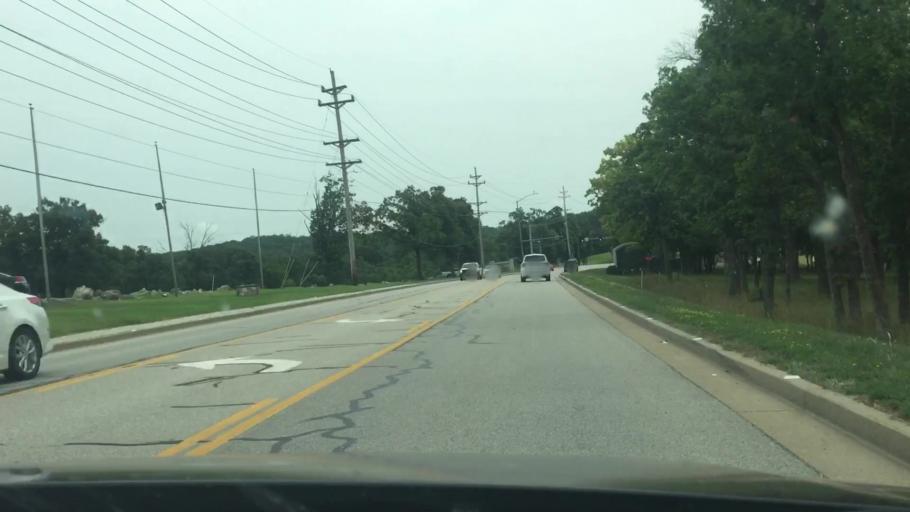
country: US
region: Missouri
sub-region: Camden County
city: Four Seasons
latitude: 38.1913
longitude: -92.6898
